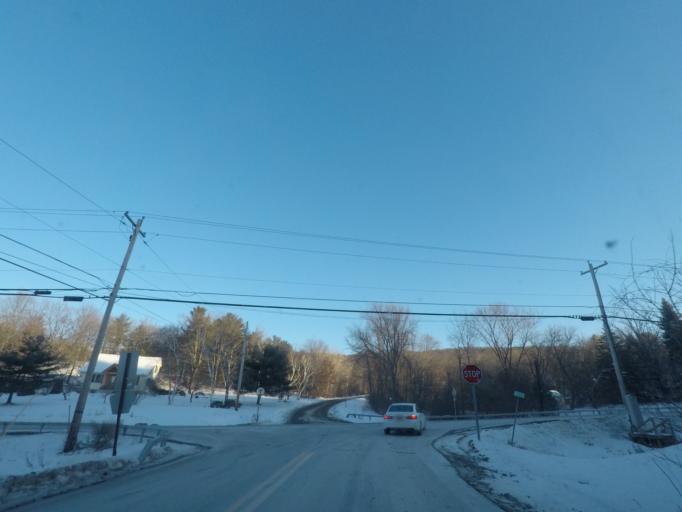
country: US
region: New York
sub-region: Saratoga County
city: Waterford
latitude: 42.8256
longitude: -73.6297
